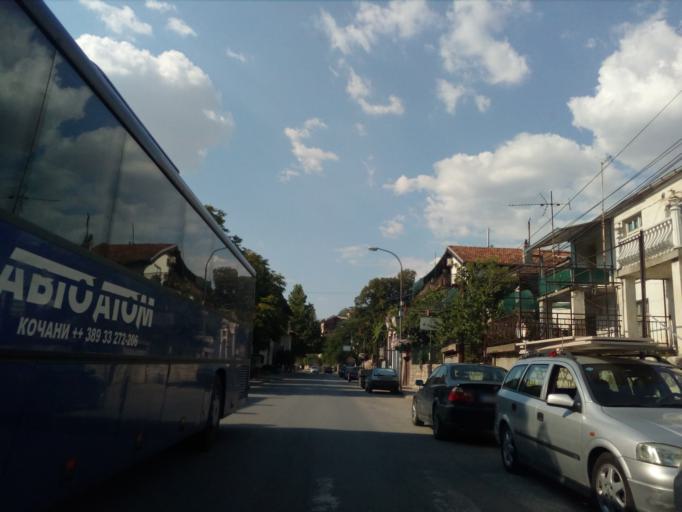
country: MK
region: Veles
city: Veles
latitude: 41.7180
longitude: 21.7882
